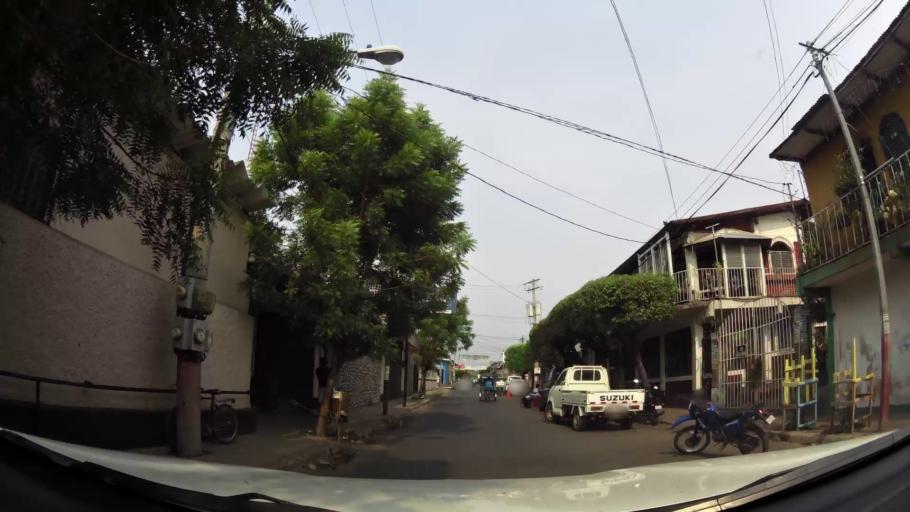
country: NI
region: Chinandega
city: Chinandega
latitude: 12.6286
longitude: -87.1289
